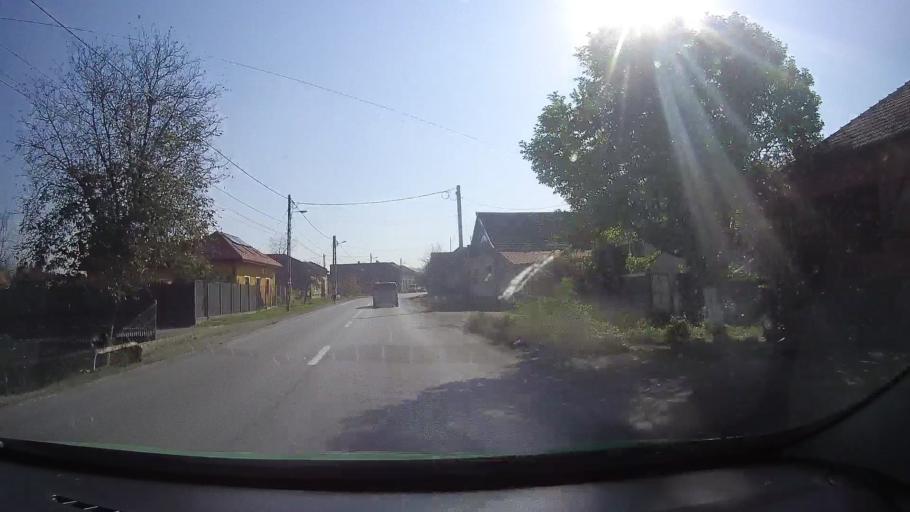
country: RO
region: Hunedoara
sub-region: Comuna Dobra
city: Dobra
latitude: 45.9163
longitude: 22.5623
